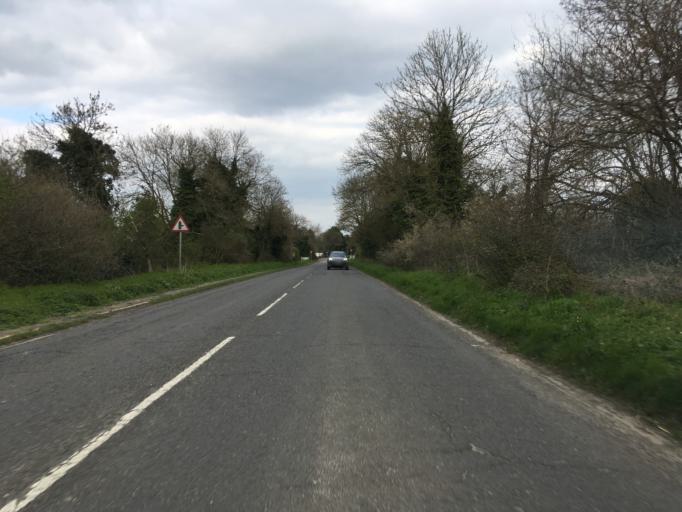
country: GB
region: England
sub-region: Oxfordshire
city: Carterton
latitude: 51.7954
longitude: -1.5547
